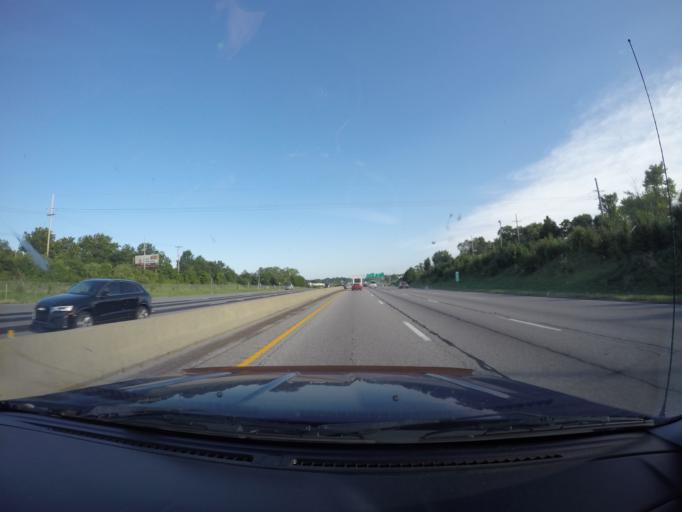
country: US
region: Missouri
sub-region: Platte County
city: Riverside
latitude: 39.2068
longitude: -94.6353
